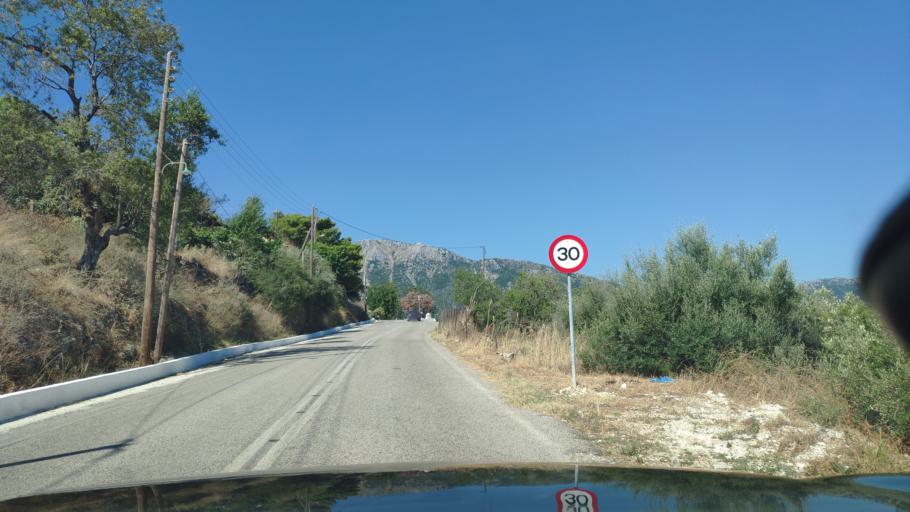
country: GR
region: Ionian Islands
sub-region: Lefkada
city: Nidri
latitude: 38.6621
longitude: 20.6004
